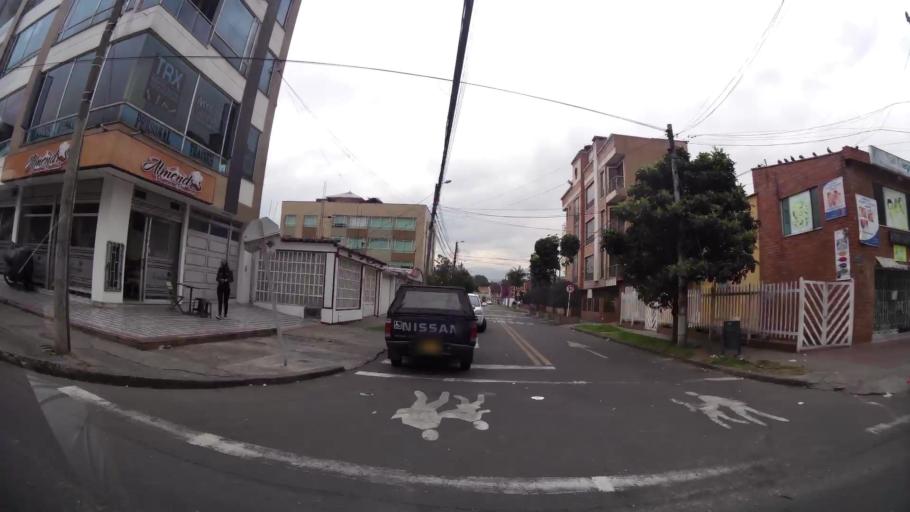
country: CO
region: Bogota D.C.
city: Bogota
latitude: 4.6682
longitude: -74.1174
